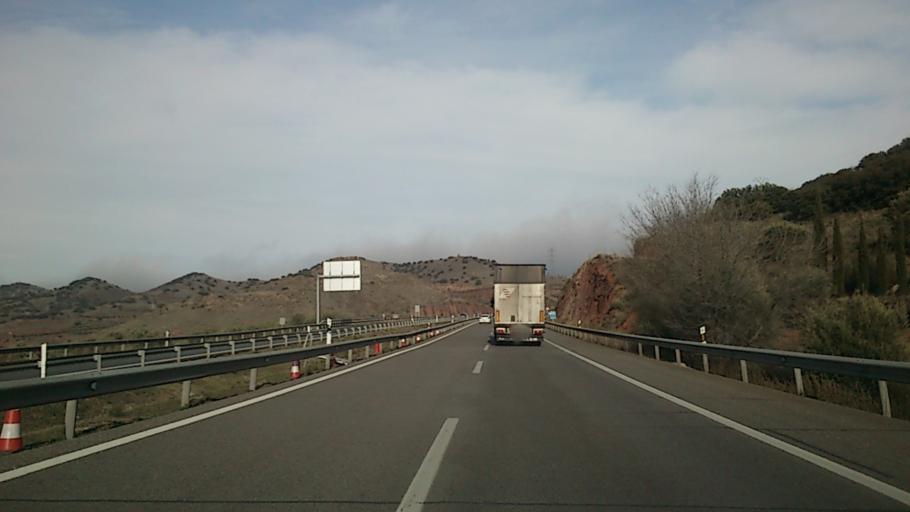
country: ES
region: Aragon
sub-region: Provincia de Zaragoza
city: Morata de Jalon
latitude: 41.4219
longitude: -1.4951
